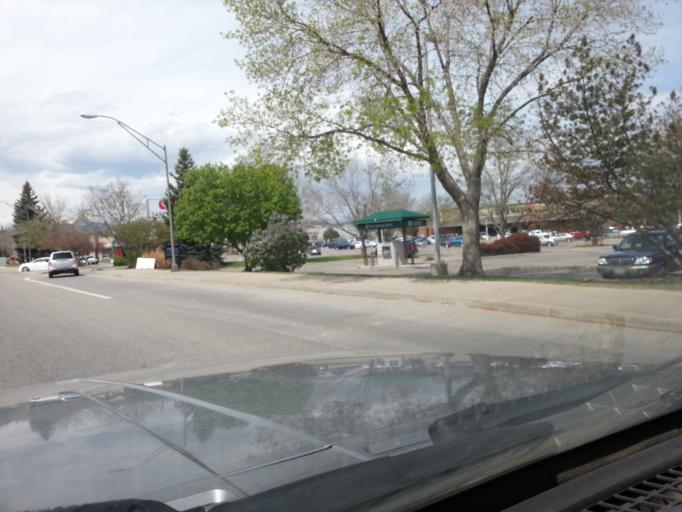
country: US
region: Colorado
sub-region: Larimer County
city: Loveland
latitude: 40.4074
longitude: -105.1084
